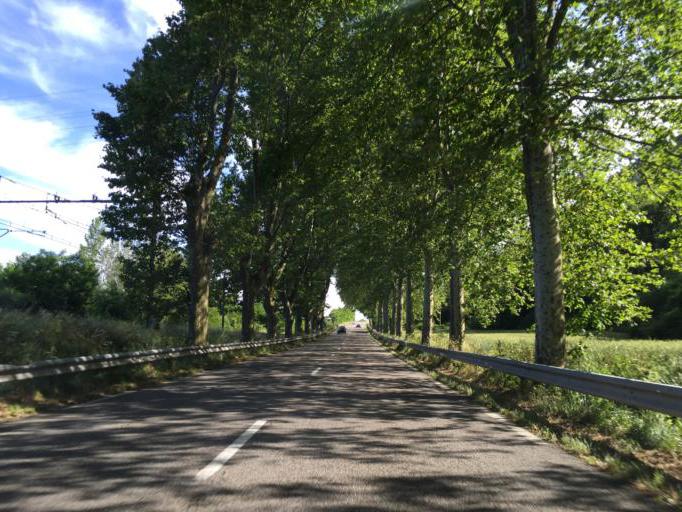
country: FR
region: Rhone-Alpes
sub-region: Departement de l'Ardeche
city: Cruas
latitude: 44.6842
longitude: 4.7719
